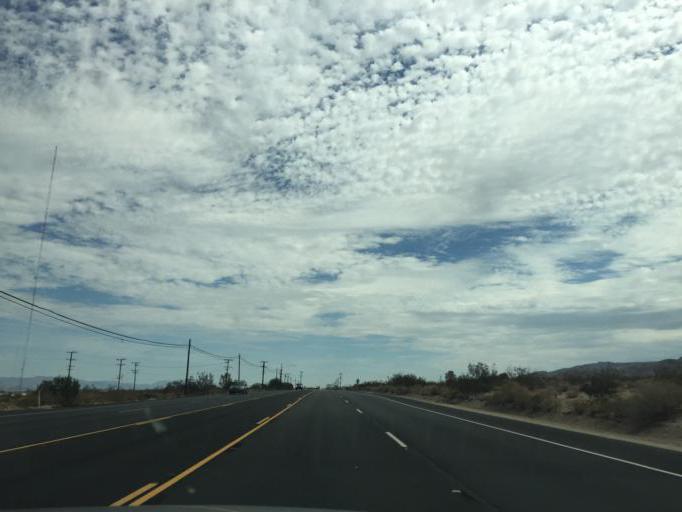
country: US
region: California
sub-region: San Bernardino County
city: Twentynine Palms
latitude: 34.1351
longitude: -116.1732
